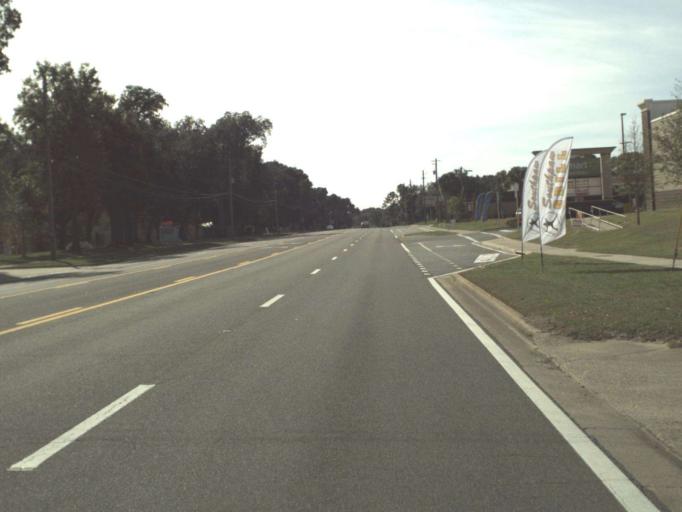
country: US
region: Florida
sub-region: Escambia County
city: Bellview
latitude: 30.4785
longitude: -87.3068
